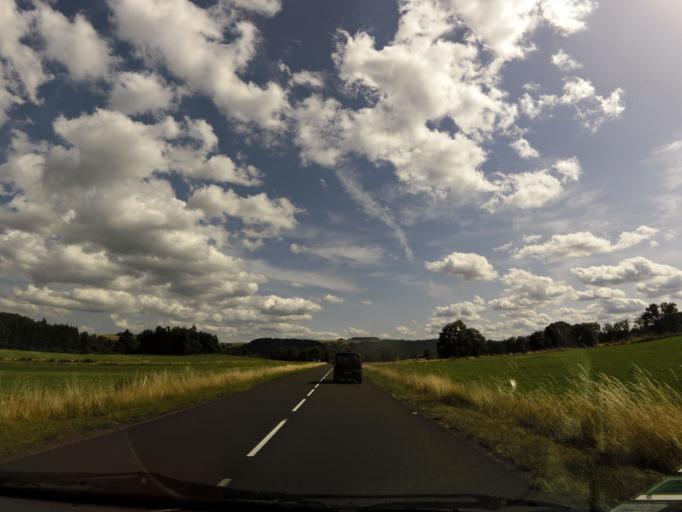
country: FR
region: Auvergne
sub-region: Departement du Puy-de-Dome
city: Aydat
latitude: 45.5307
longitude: 2.9468
